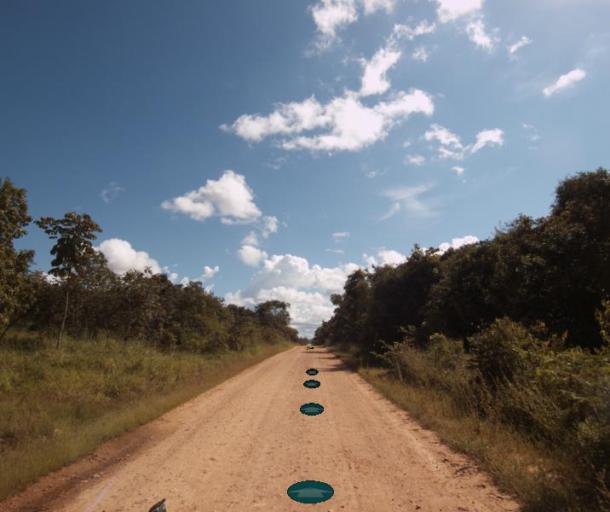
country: BR
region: Goias
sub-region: Pirenopolis
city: Pirenopolis
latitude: -15.7842
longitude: -49.0559
